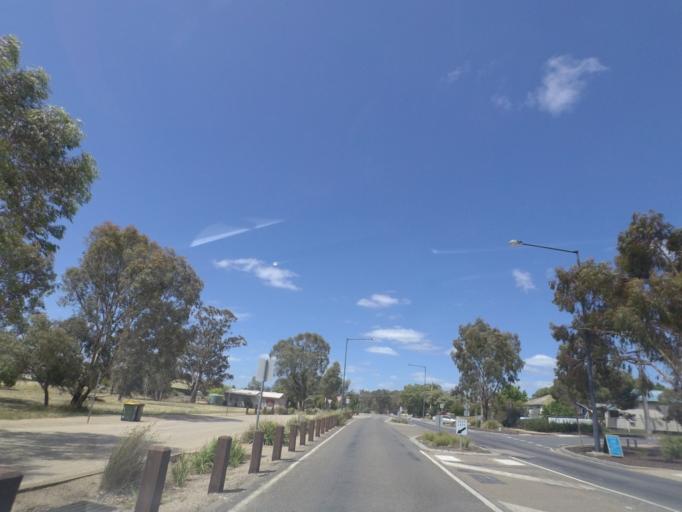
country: AU
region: Victoria
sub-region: Wangaratta
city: Wangaratta
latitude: -36.4636
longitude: 146.2247
